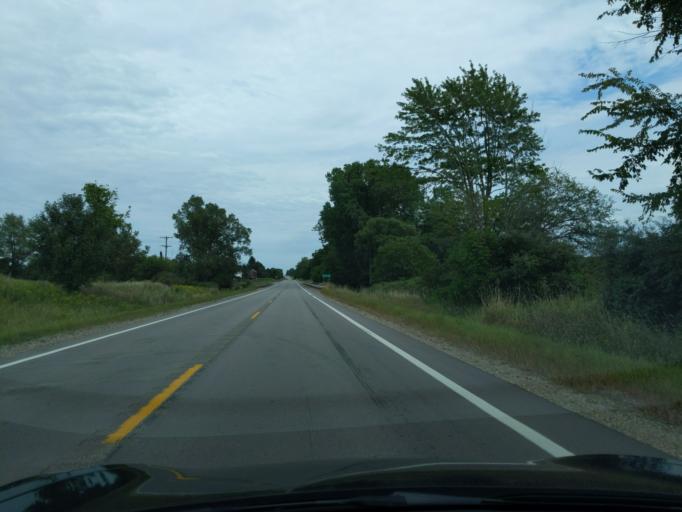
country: US
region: Michigan
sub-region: Barry County
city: Nashville
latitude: 42.5672
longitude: -85.0568
